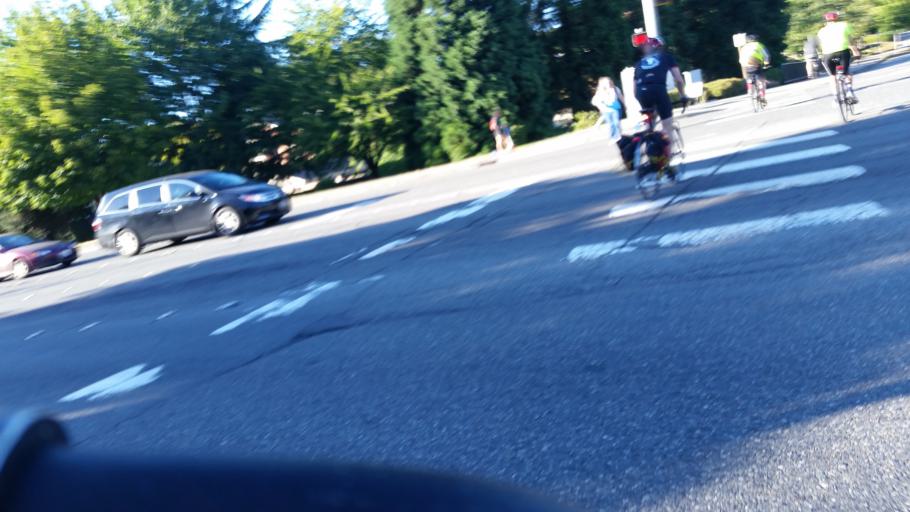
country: US
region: Washington
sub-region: King County
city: Redmond
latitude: 47.6693
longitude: -122.1298
